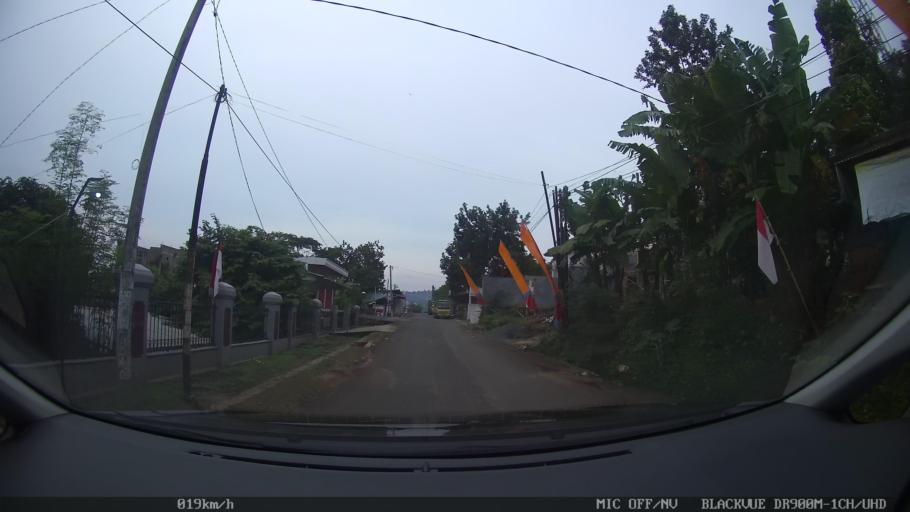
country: ID
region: Lampung
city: Kedaton
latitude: -5.4020
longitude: 105.2418
